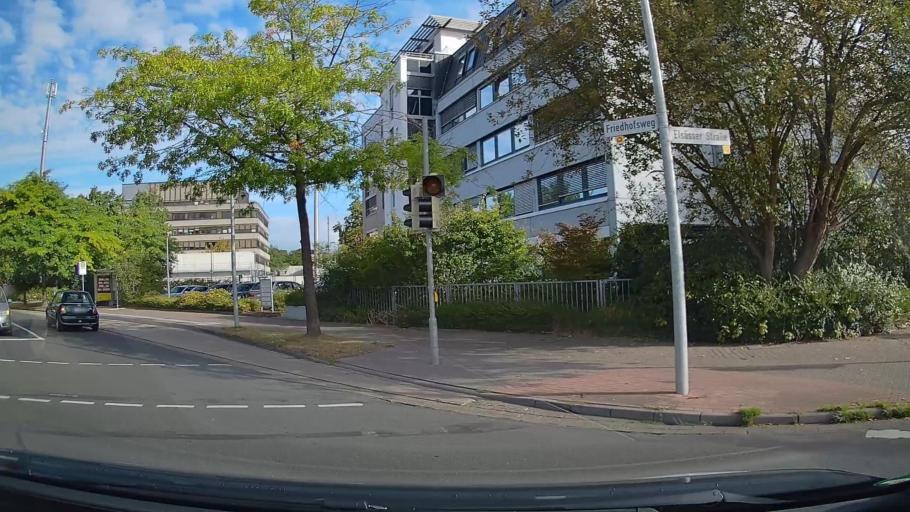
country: DE
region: Lower Saxony
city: Oldenburg
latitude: 53.1514
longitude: 8.2006
